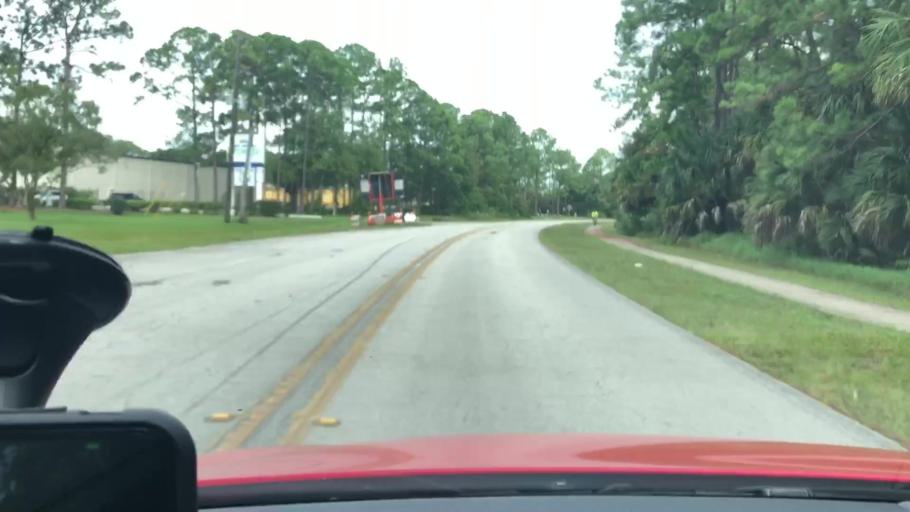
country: US
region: Florida
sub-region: Volusia County
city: Holly Hill
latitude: 29.2119
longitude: -81.0698
